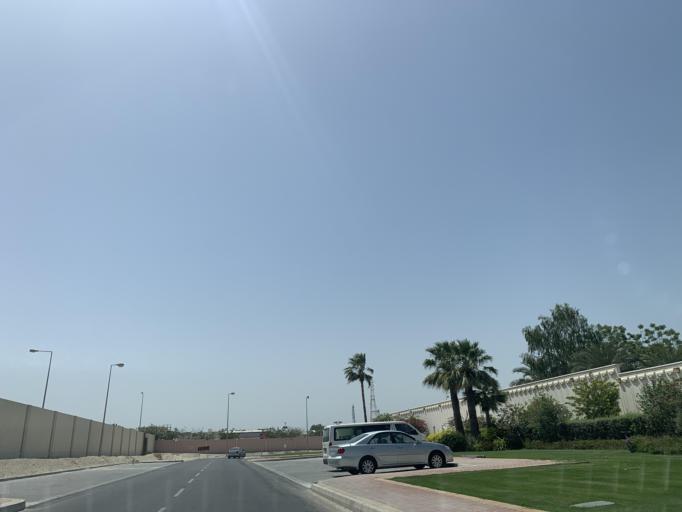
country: BH
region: Northern
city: Ar Rifa'
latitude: 26.1427
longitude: 50.5521
